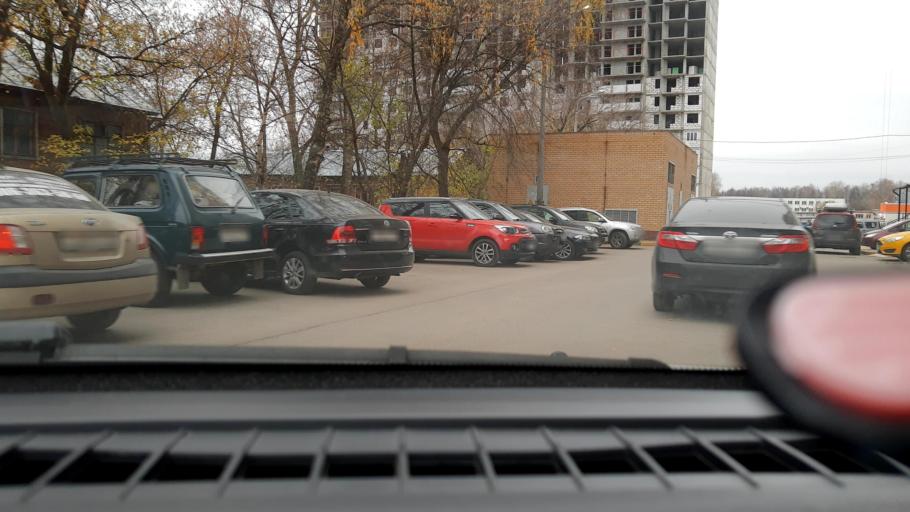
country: RU
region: Nizjnij Novgorod
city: Nizhniy Novgorod
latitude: 56.3046
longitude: 43.9974
